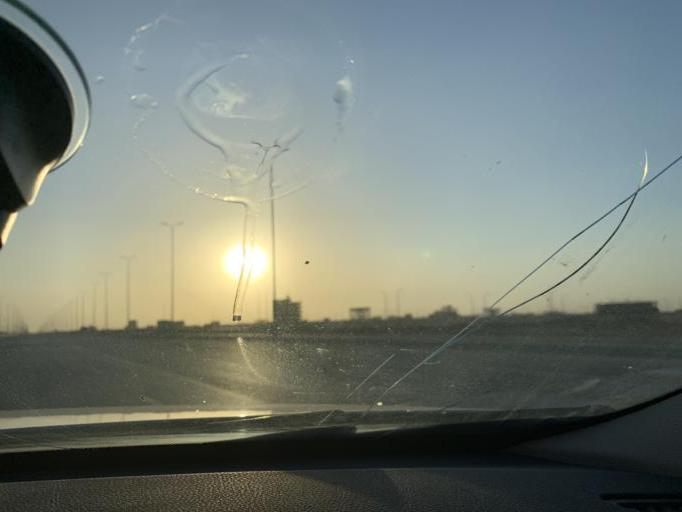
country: EG
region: Muhafazat al Qalyubiyah
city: Al Khankah
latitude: 30.0269
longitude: 31.5798
